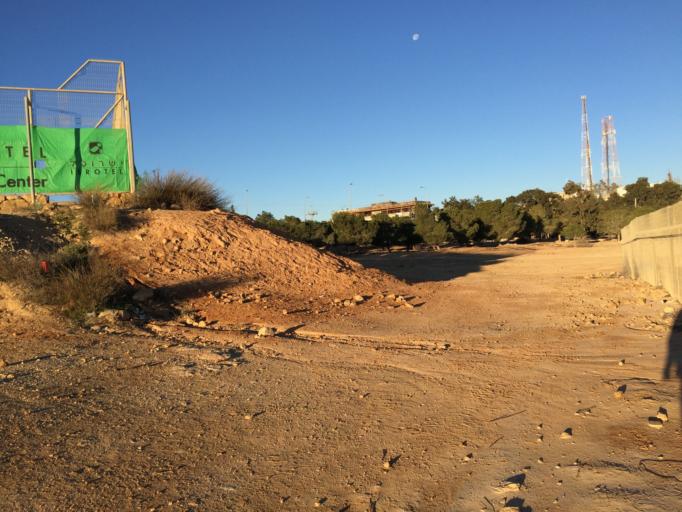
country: IL
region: Southern District
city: Mitzpe Ramon
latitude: 30.6131
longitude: 34.8058
